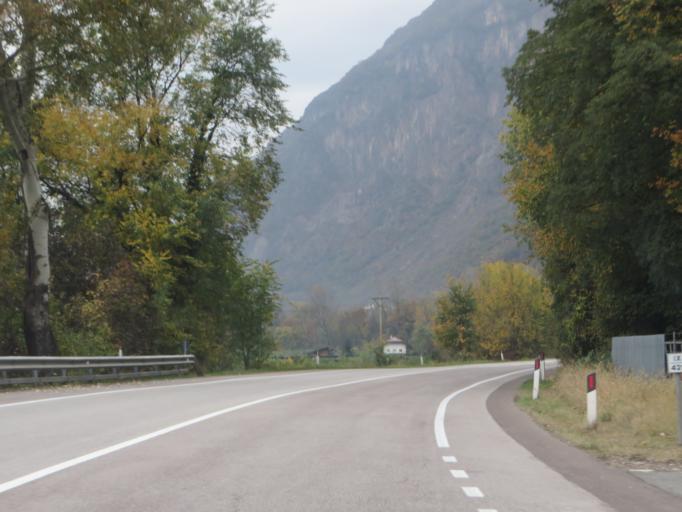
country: IT
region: Trentino-Alto Adige
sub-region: Bolzano
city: Ora
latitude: 46.3644
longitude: 11.3152
